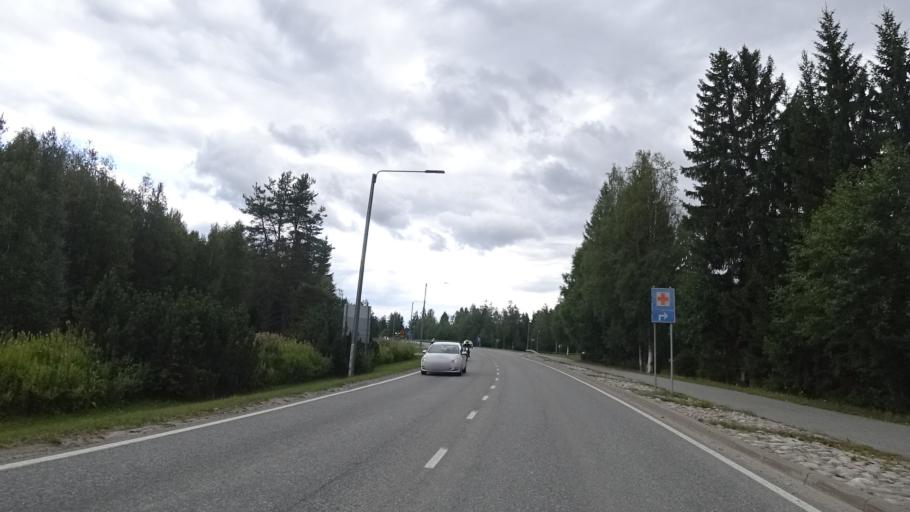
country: FI
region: North Karelia
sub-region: Joensuu
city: Ilomantsi
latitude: 62.6670
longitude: 30.9375
